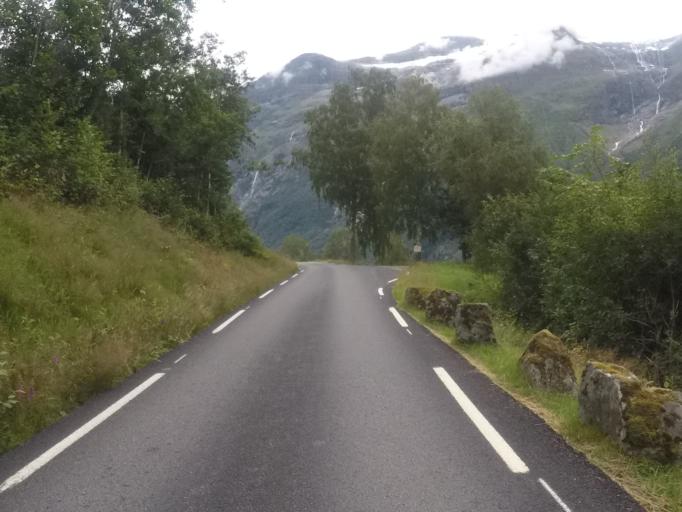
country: NO
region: Sogn og Fjordane
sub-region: Stryn
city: Stryn
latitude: 61.8350
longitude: 6.9490
